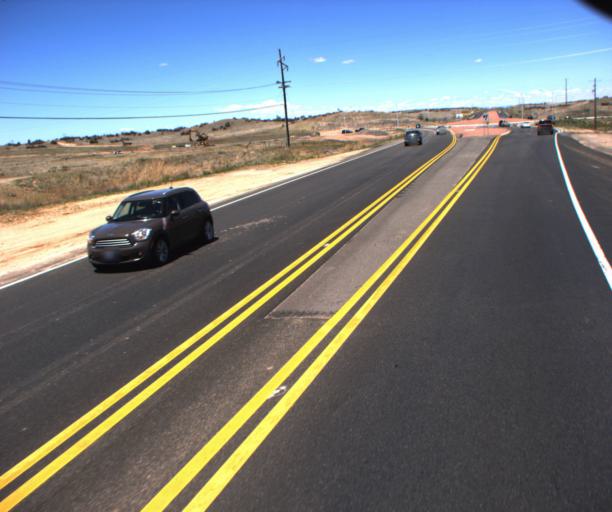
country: US
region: Arizona
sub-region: Yavapai County
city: Chino Valley
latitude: 34.6502
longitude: -112.4342
